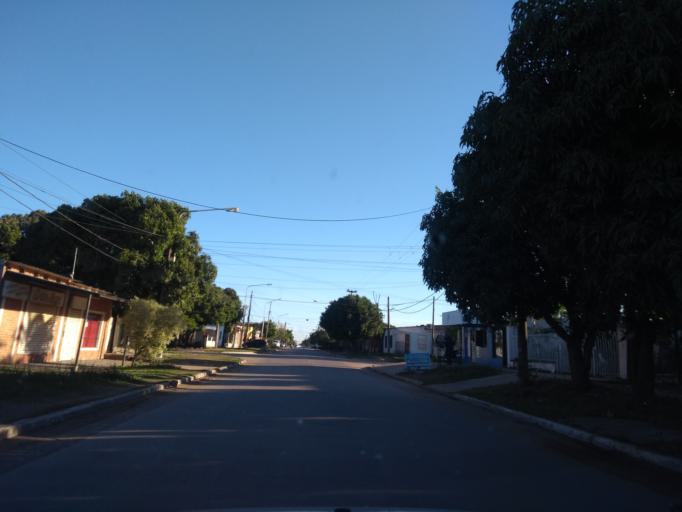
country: AR
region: Chaco
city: Barranqueras
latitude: -27.4899
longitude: -58.9474
